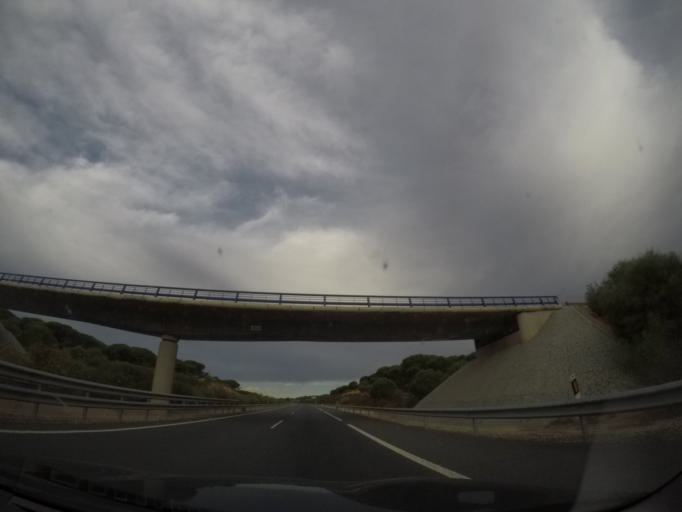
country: ES
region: Andalusia
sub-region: Provincia de Huelva
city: Cartaya
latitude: 37.3229
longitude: -7.0937
